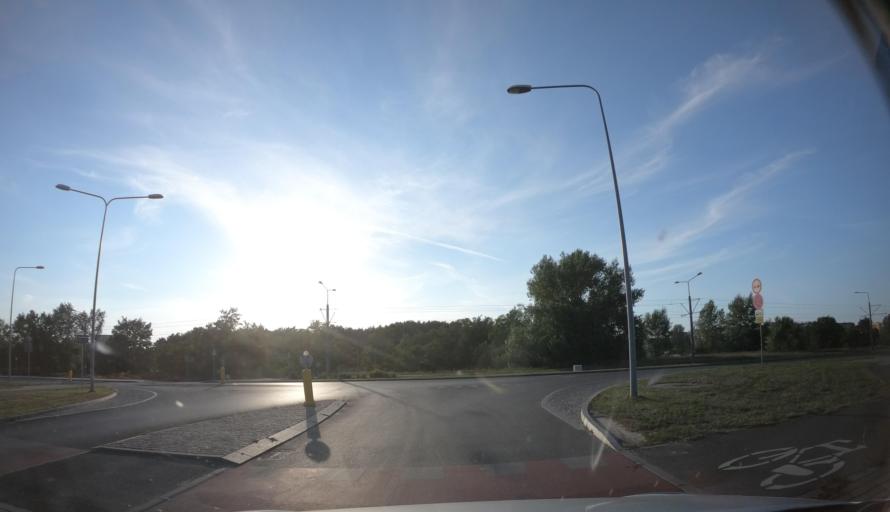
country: PL
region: Kujawsko-Pomorskie
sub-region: Bydgoszcz
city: Fordon
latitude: 53.1541
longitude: 18.1613
